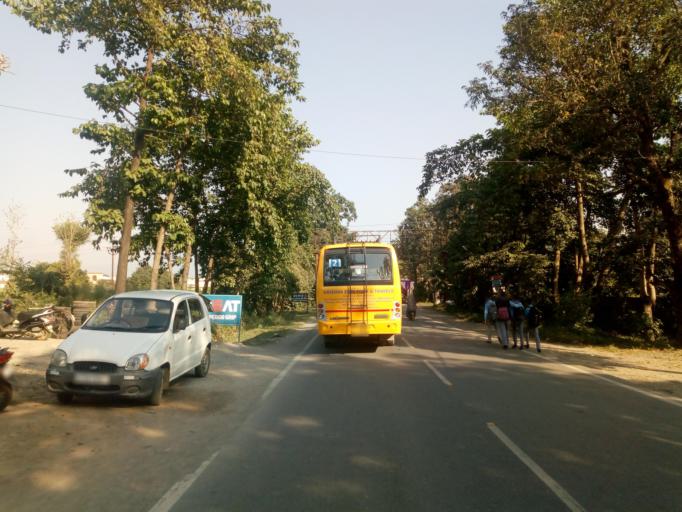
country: IN
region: Uttarakhand
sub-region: Dehradun
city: Harbatpur
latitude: 30.4413
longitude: 77.7290
